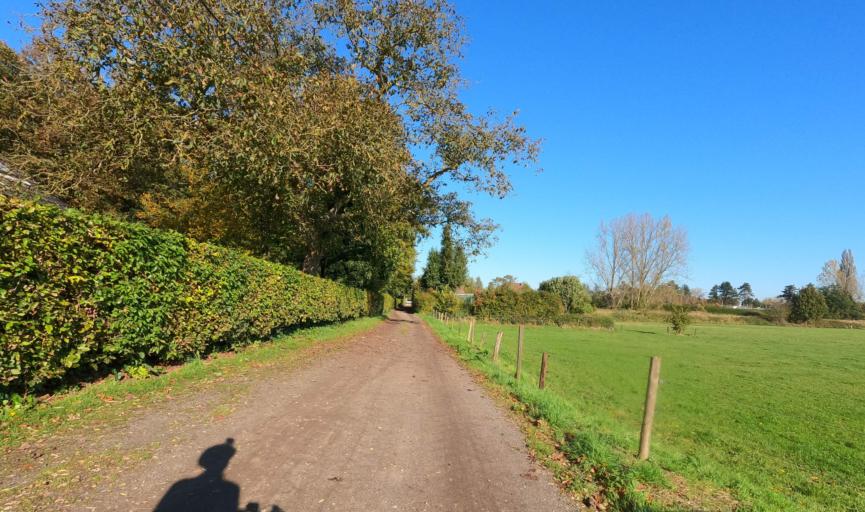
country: BE
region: Flanders
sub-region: Provincie Antwerpen
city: Heist-op-den-Berg
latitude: 51.0987
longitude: 4.7341
